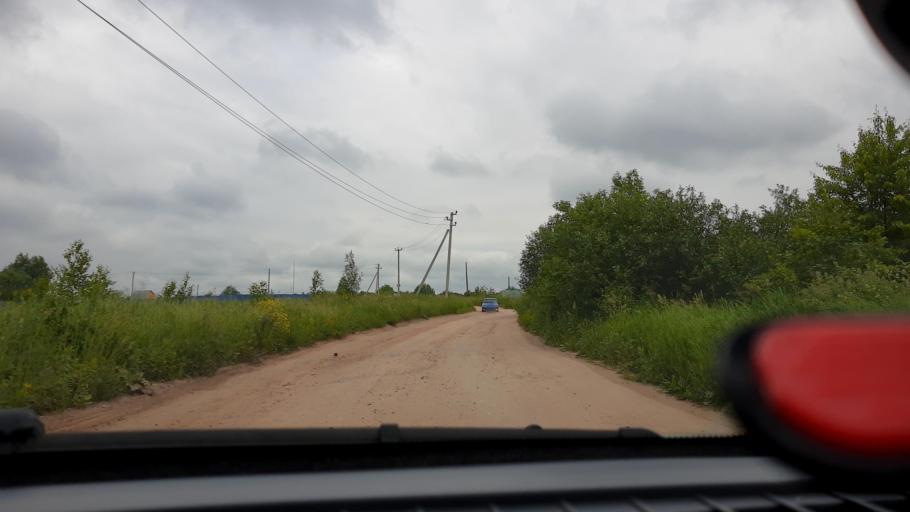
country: RU
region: Nizjnij Novgorod
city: Burevestnik
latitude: 56.1014
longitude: 43.9388
